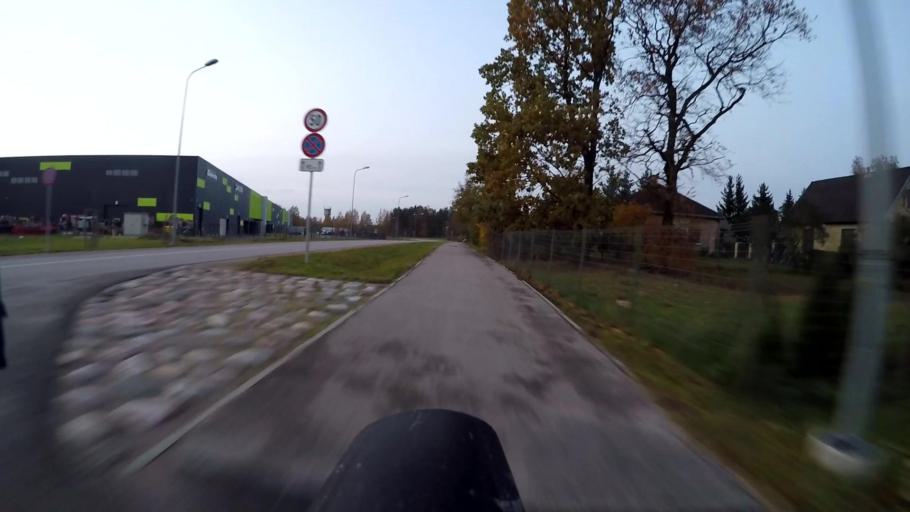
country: LV
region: Marupe
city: Marupe
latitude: 56.9165
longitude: 23.9919
